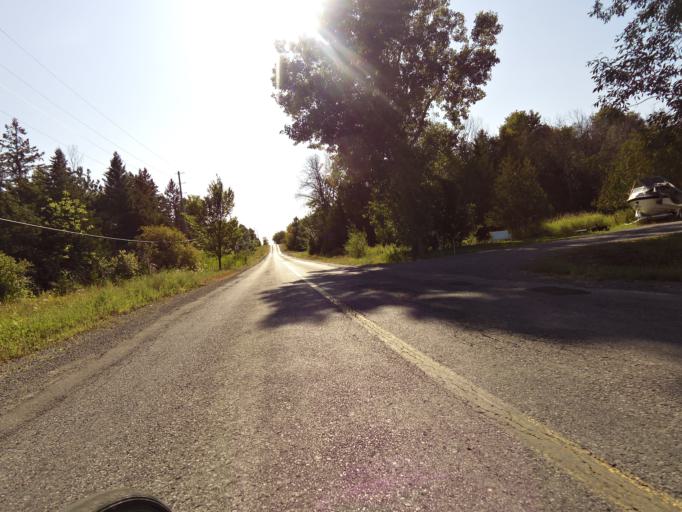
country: CA
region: Ontario
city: Bells Corners
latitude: 45.4559
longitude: -75.9664
